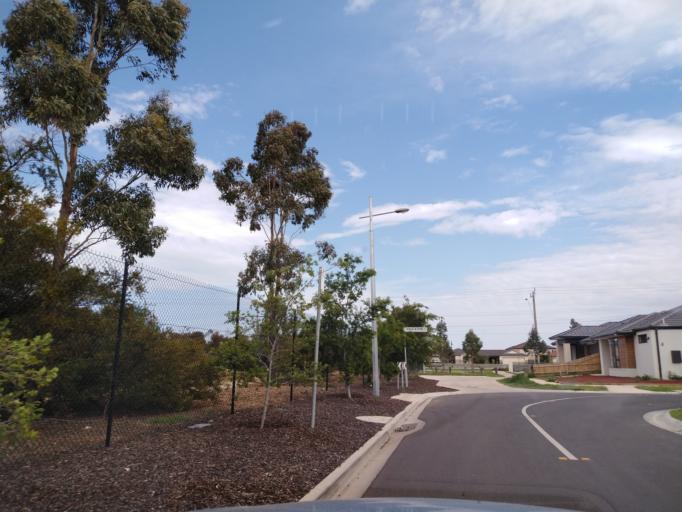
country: AU
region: Victoria
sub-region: Wyndham
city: Williams Landing
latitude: -37.8507
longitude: 144.7166
